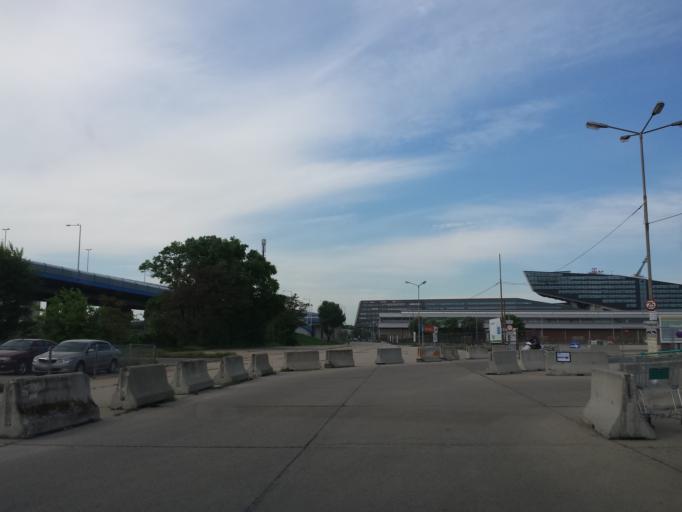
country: AT
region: Vienna
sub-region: Wien Stadt
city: Vienna
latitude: 48.1896
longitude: 16.4096
